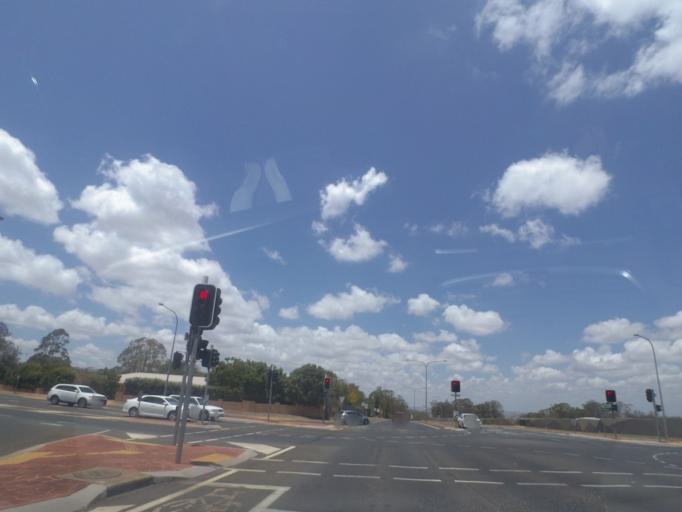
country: AU
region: Queensland
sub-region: Toowoomba
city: Darling Heights
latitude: -27.6114
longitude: 151.9451
